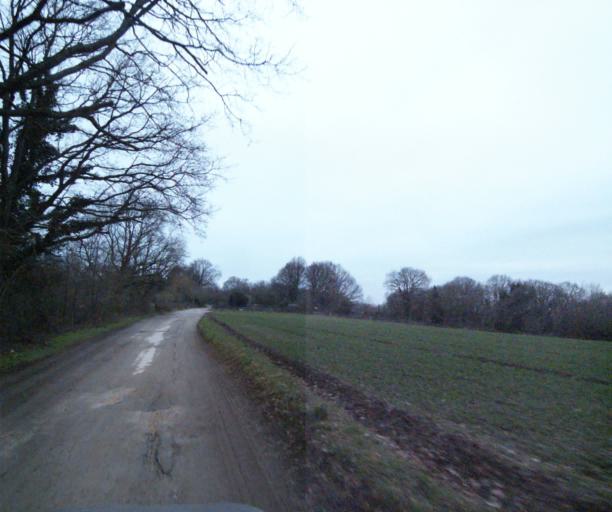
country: FR
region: Ile-de-France
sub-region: Departement de Seine-et-Marne
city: Longperrier
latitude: 49.0620
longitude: 2.6599
